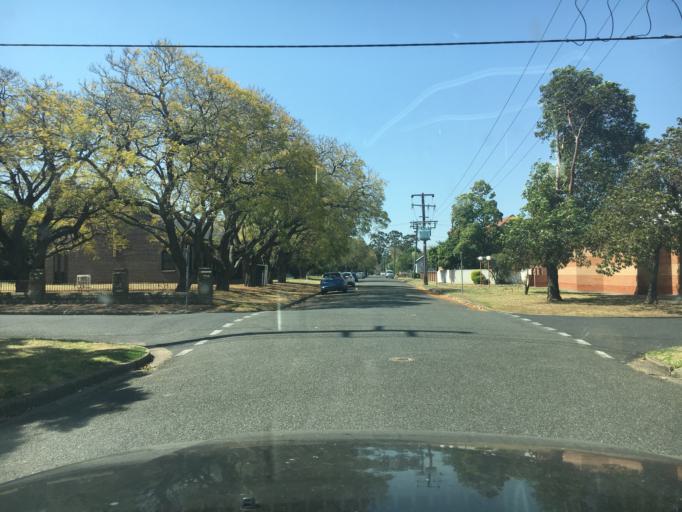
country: AU
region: New South Wales
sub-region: Singleton
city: Singleton
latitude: -32.5640
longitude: 151.1778
